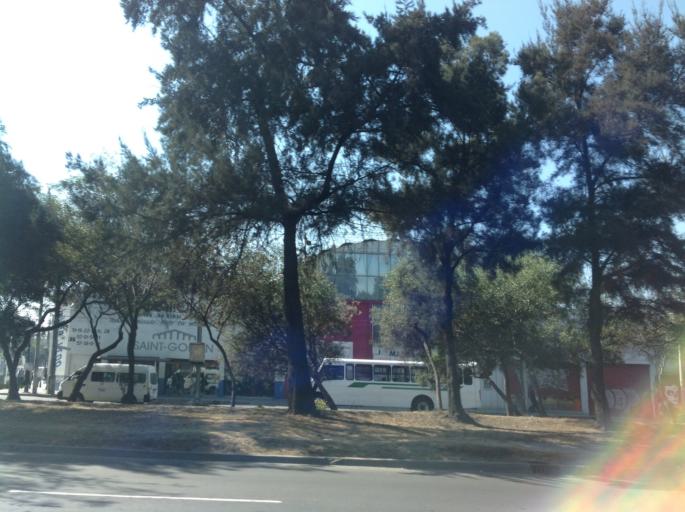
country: MX
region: Mexico City
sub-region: Iztacalco
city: Iztacalco
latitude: 19.4039
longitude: -99.0687
